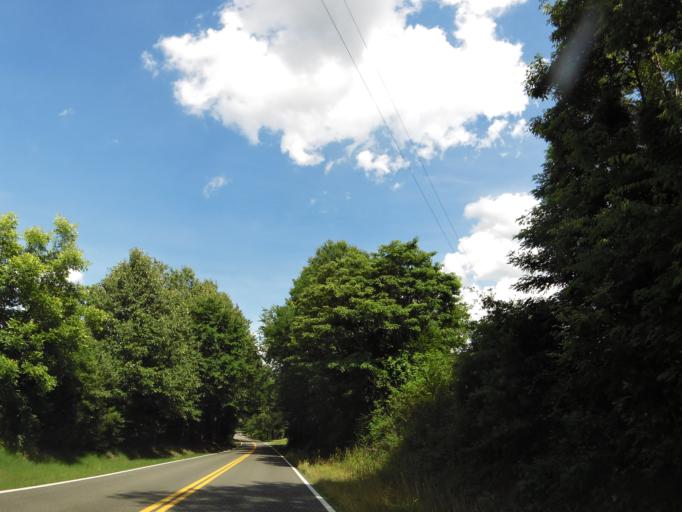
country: US
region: Tennessee
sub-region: Gibson County
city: Milan
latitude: 35.9764
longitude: -88.7923
